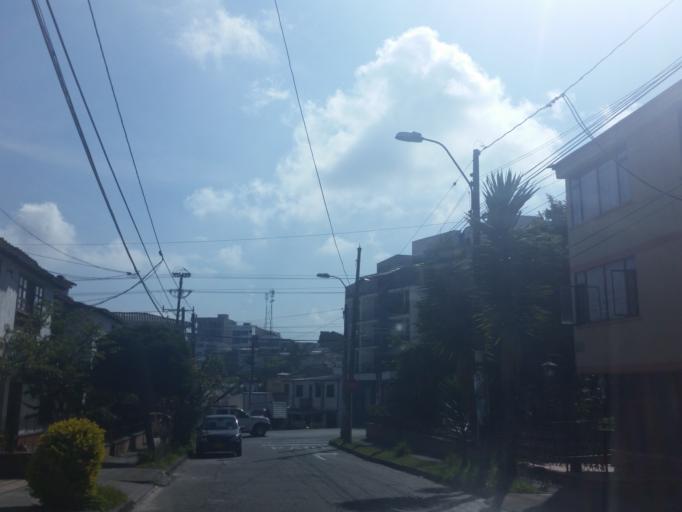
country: CO
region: Caldas
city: Manizales
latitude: 5.0761
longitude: -75.5266
